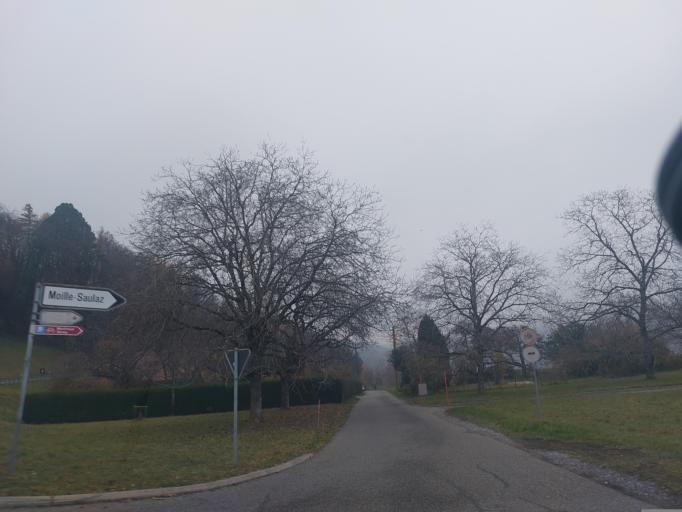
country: CH
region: Fribourg
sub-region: Veveyse District
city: Attalens
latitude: 46.4941
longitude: 6.8706
